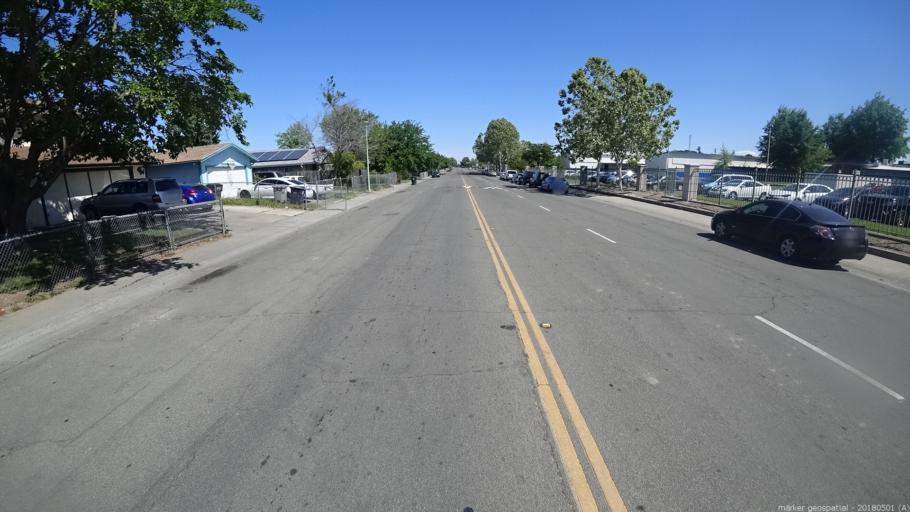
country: US
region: California
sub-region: Sacramento County
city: Rio Linda
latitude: 38.6333
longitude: -121.4385
